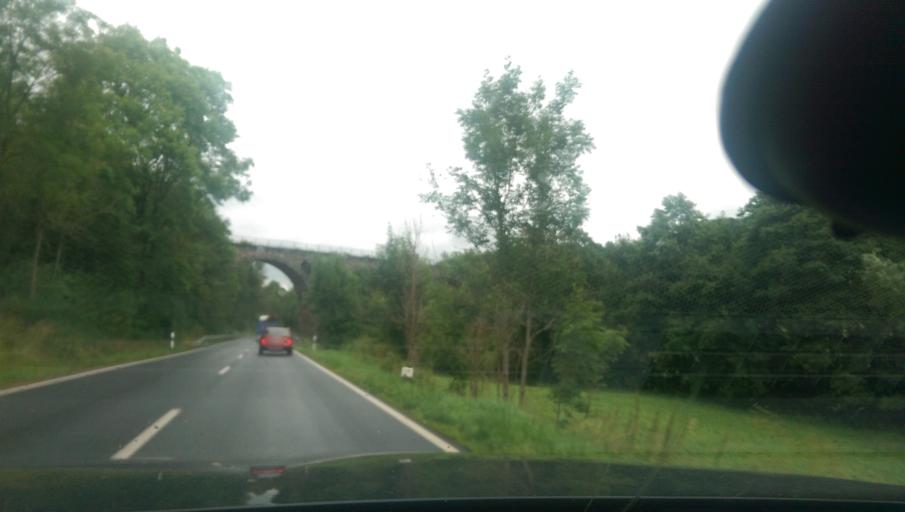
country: DE
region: Hesse
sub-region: Regierungsbezirk Kassel
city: Grossalmerode
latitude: 51.2543
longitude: 9.8284
